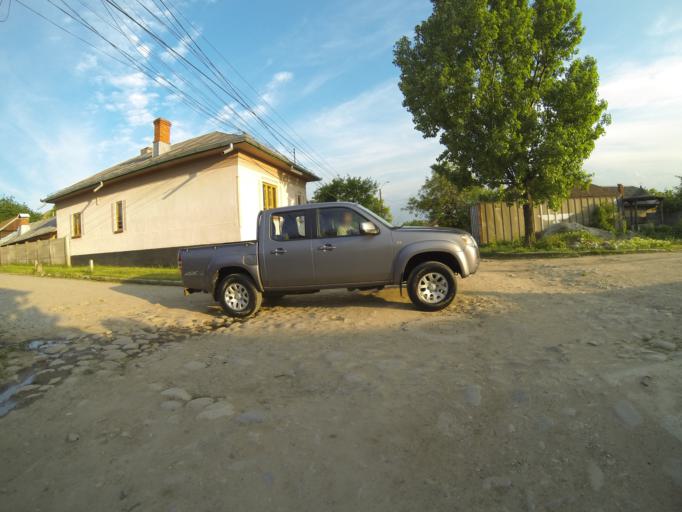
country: RO
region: Dolj
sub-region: Comuna Segarcea
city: Segarcea
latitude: 44.0950
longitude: 23.7491
